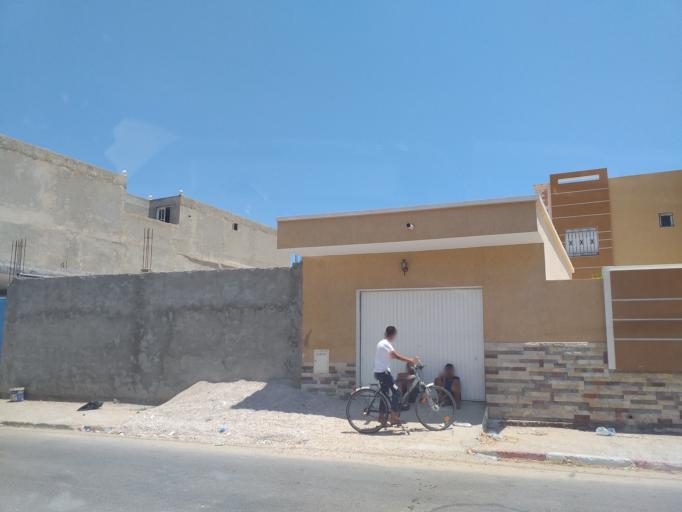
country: TN
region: Qabis
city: Gabes
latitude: 33.9453
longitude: 10.0618
